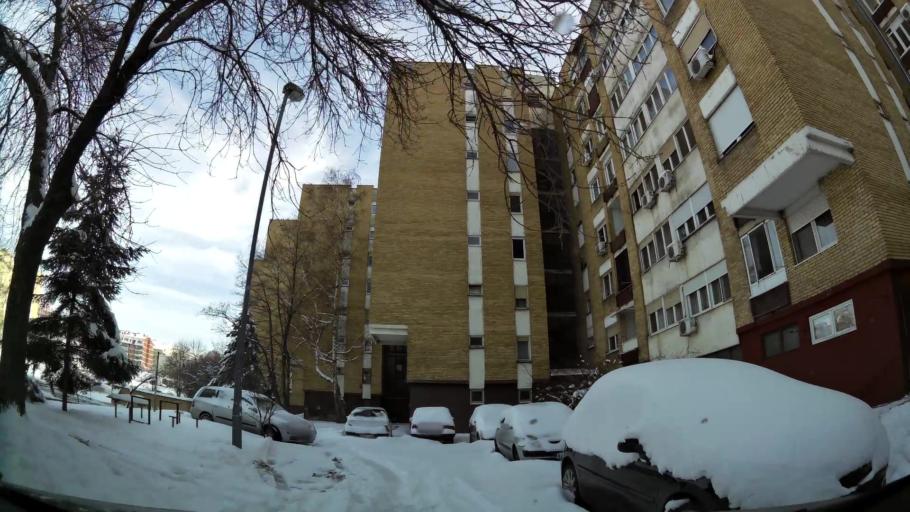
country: RS
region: Central Serbia
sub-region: Belgrade
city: Zvezdara
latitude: 44.7888
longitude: 20.5363
